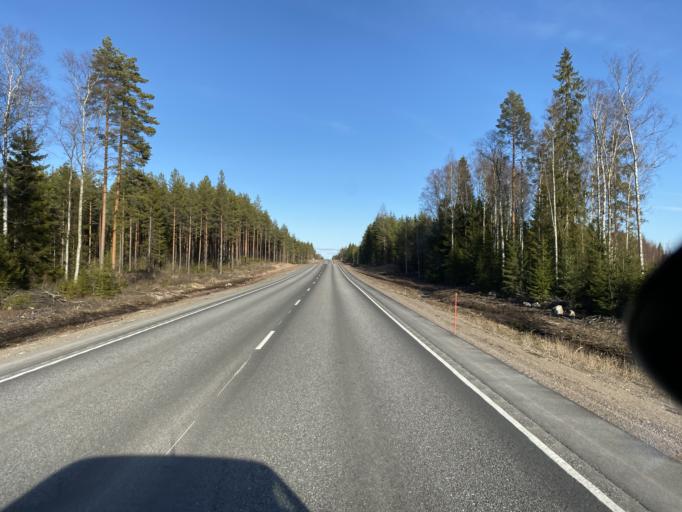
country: FI
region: Satakunta
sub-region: Rauma
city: Koeylioe
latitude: 61.1652
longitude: 22.3692
